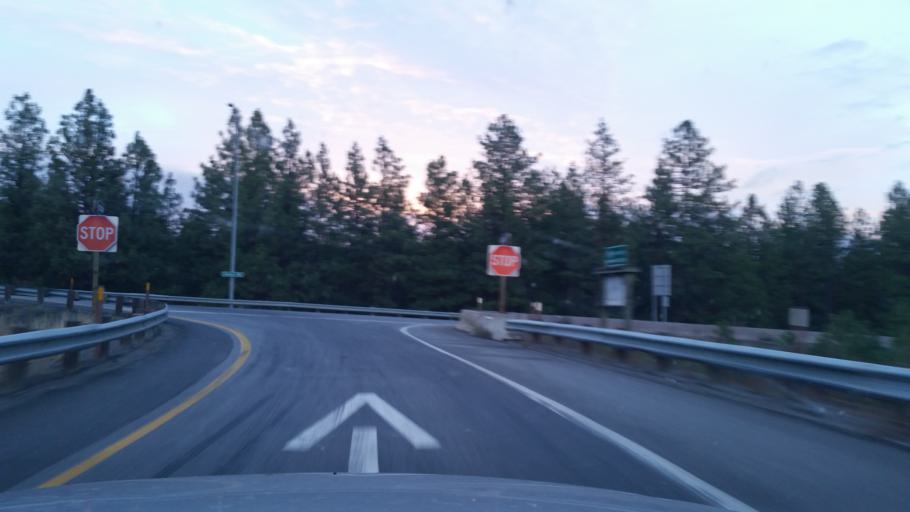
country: US
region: Washington
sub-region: Spokane County
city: Spokane
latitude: 47.6180
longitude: -117.5012
